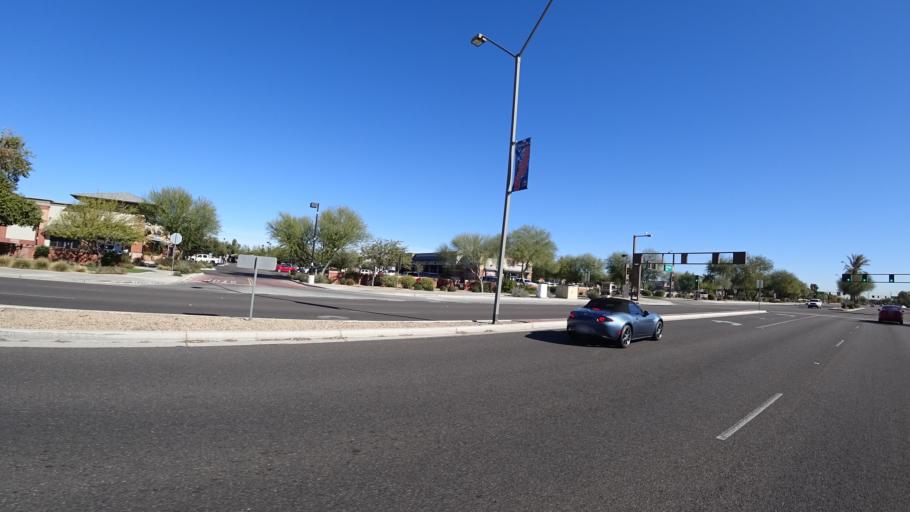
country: US
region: Arizona
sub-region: Maricopa County
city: Litchfield Park
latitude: 33.4858
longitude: -112.3657
